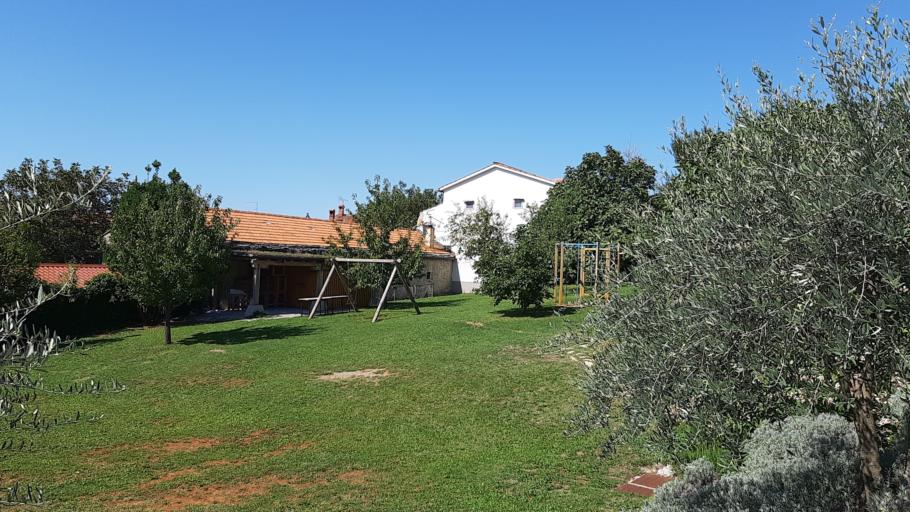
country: IT
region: Friuli Venezia Giulia
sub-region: Provincia di Trieste
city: Sgonico
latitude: 45.7711
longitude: 13.7836
